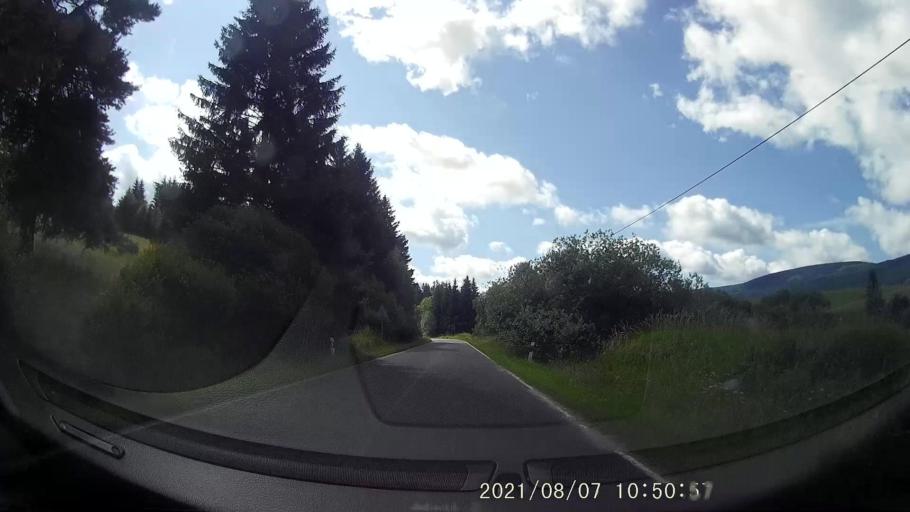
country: PL
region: Lower Silesian Voivodeship
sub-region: Powiat klodzki
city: Polanica-Zdroj
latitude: 50.2930
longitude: 16.4668
